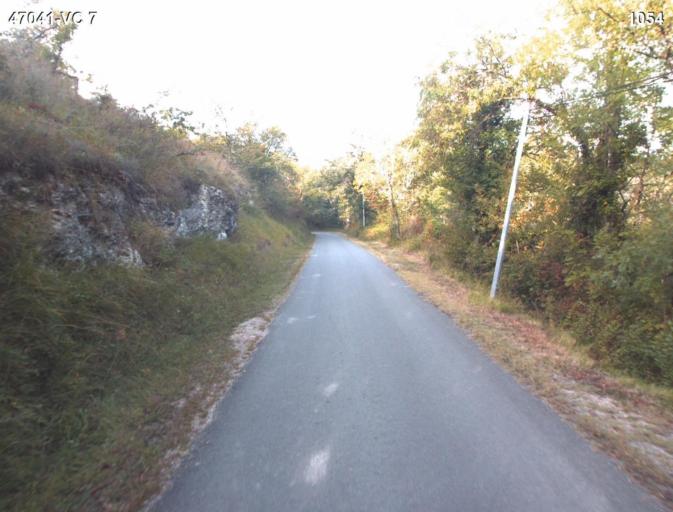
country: FR
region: Aquitaine
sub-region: Departement du Lot-et-Garonne
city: Port-Sainte-Marie
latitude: 44.1982
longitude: 0.4133
